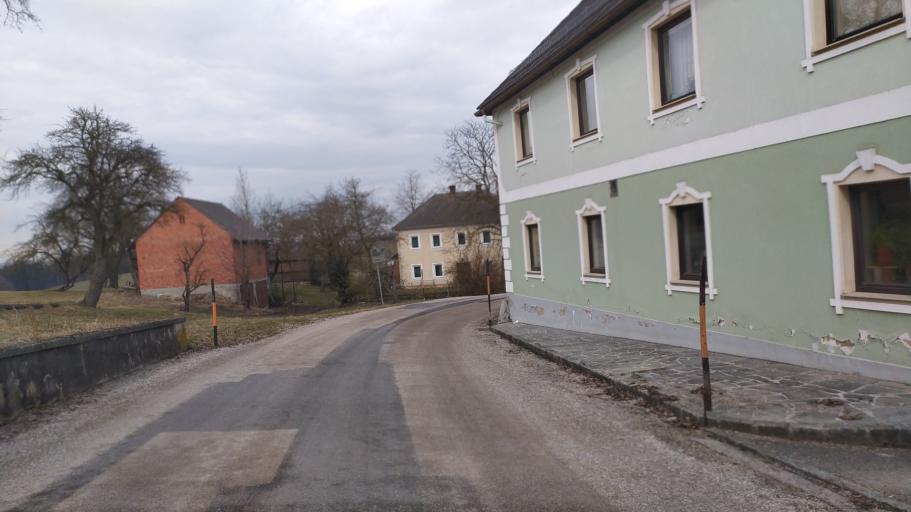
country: AT
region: Lower Austria
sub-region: Politischer Bezirk Amstetten
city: Strengberg
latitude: 48.1372
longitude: 14.7156
